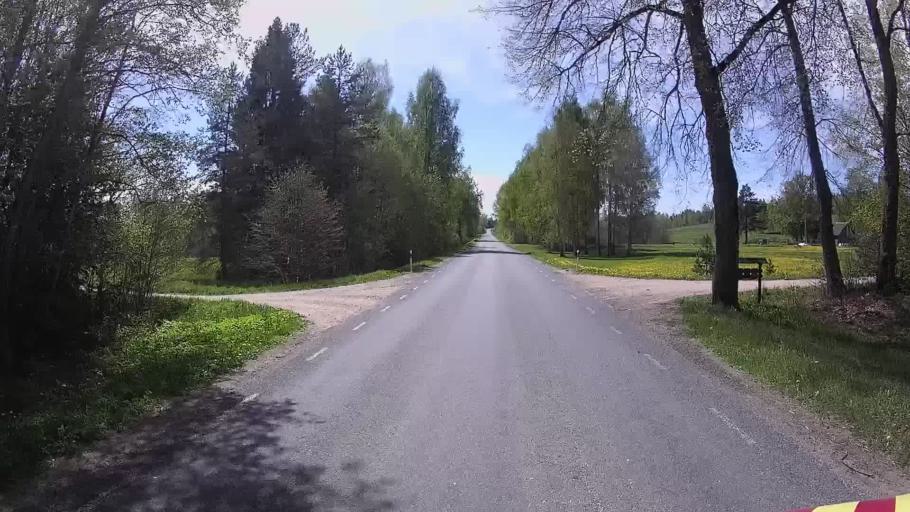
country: LV
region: Apes Novads
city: Ape
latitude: 57.6152
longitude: 26.5833
